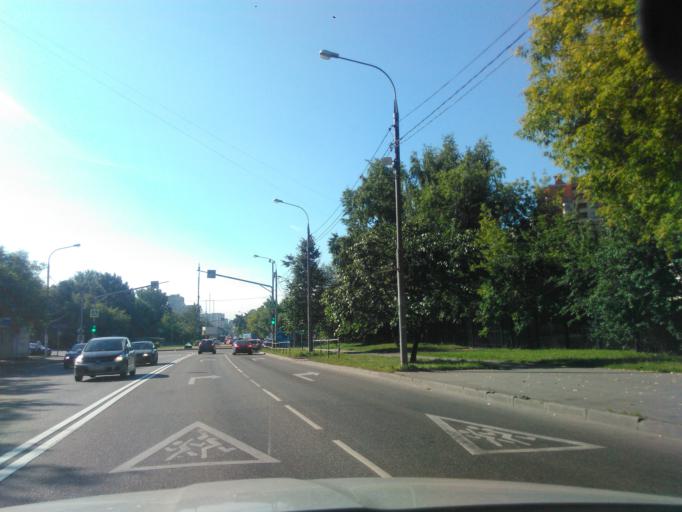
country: RU
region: Moscow
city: Novokhovrino
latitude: 55.8631
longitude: 37.5037
